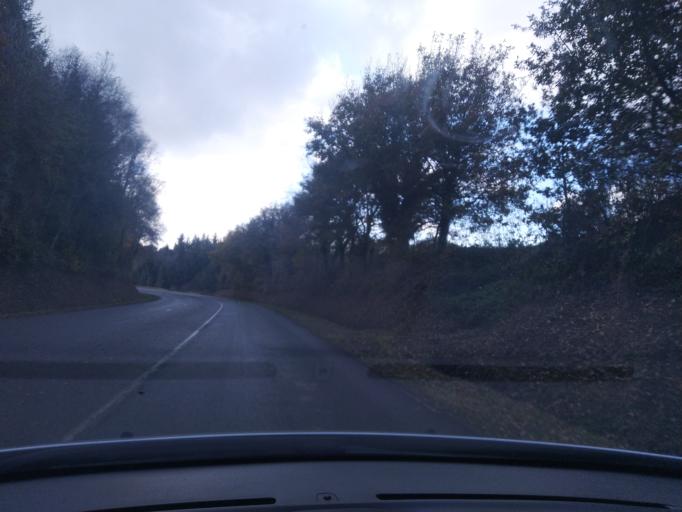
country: FR
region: Brittany
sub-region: Departement du Finistere
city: Guerlesquin
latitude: 48.5623
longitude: -3.6219
